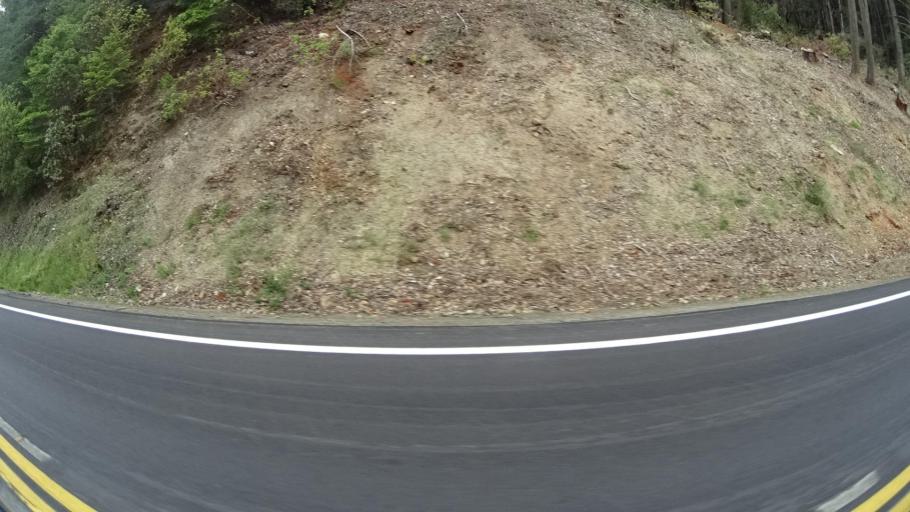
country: US
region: California
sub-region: Humboldt County
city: Willow Creek
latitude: 40.9956
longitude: -123.6298
